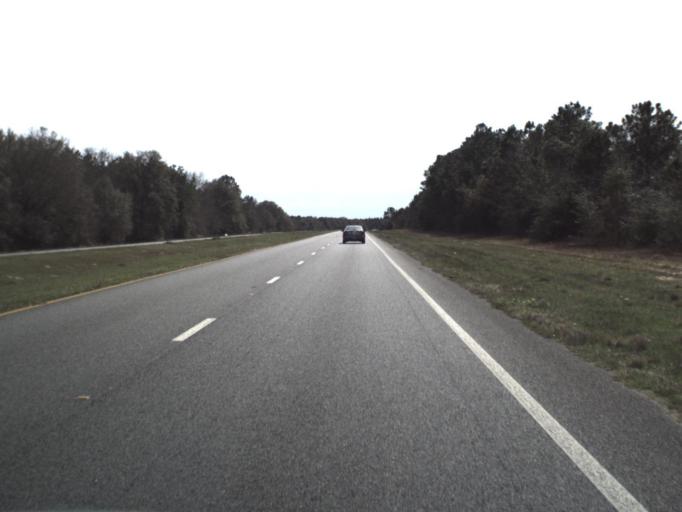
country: US
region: Florida
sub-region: Washington County
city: Chipley
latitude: 30.6216
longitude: -85.3973
